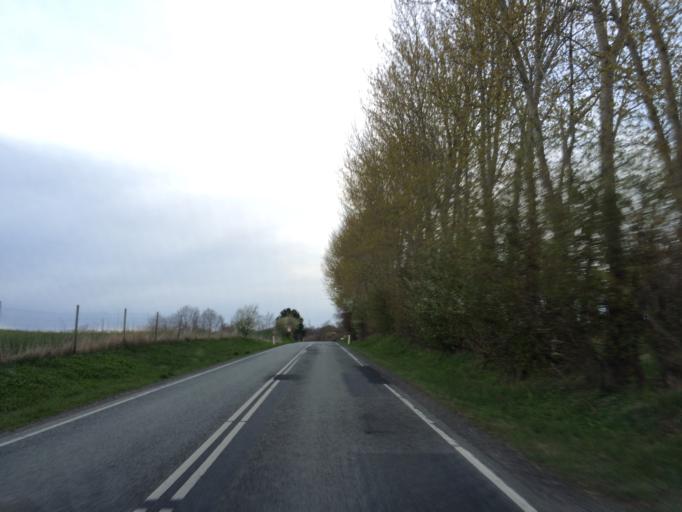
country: DK
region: South Denmark
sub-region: Odense Kommune
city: Bellinge
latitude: 55.3666
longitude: 10.2671
